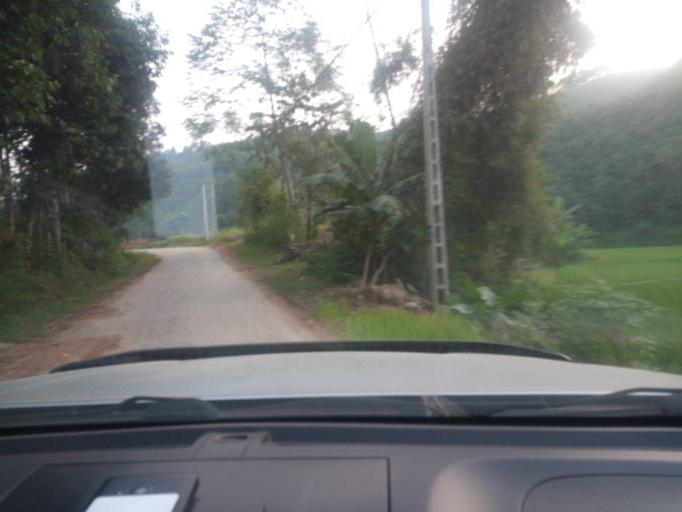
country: VN
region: Yen Bai
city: Co Phuc
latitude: 21.8274
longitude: 104.6245
